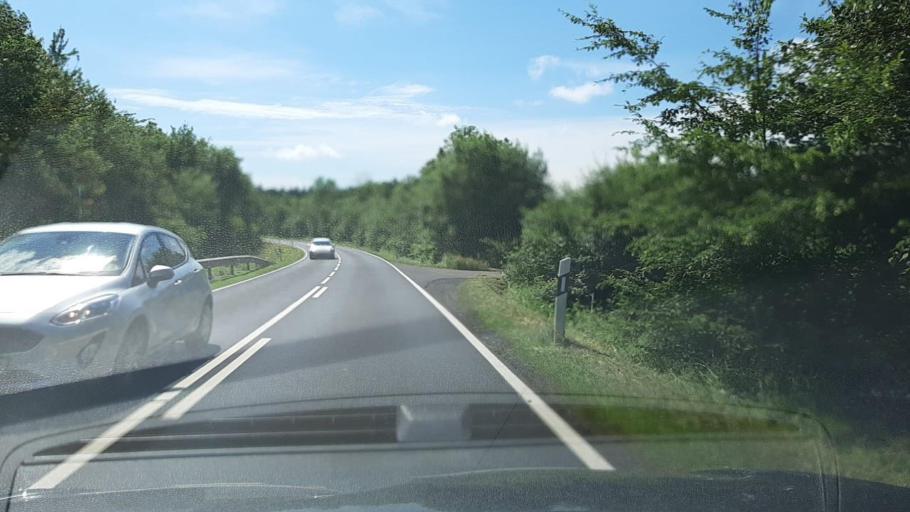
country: DE
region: Rheinland-Pfalz
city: Ediger-Eller
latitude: 50.1140
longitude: 7.1698
